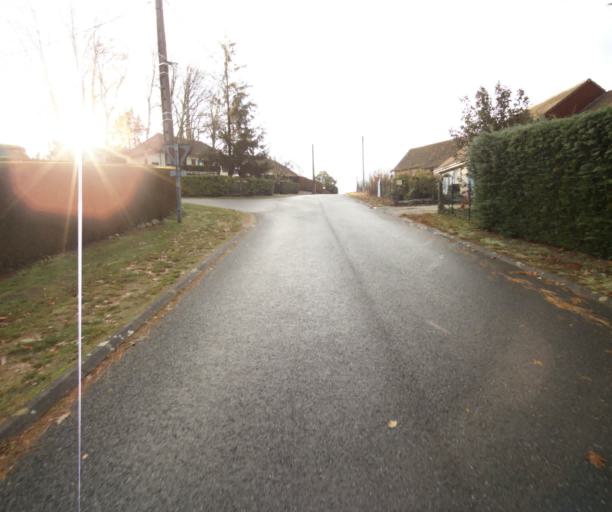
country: FR
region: Limousin
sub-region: Departement de la Correze
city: Saint-Mexant
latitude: 45.2680
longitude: 1.6412
